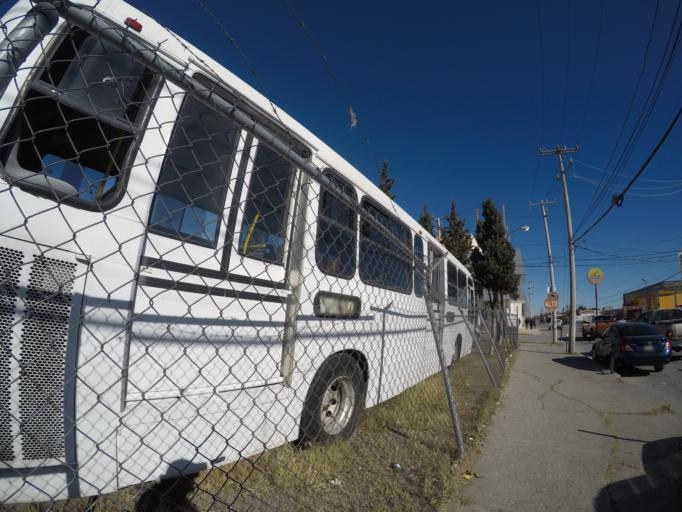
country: MX
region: Chihuahua
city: Ciudad Juarez
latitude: 31.7348
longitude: -106.4607
